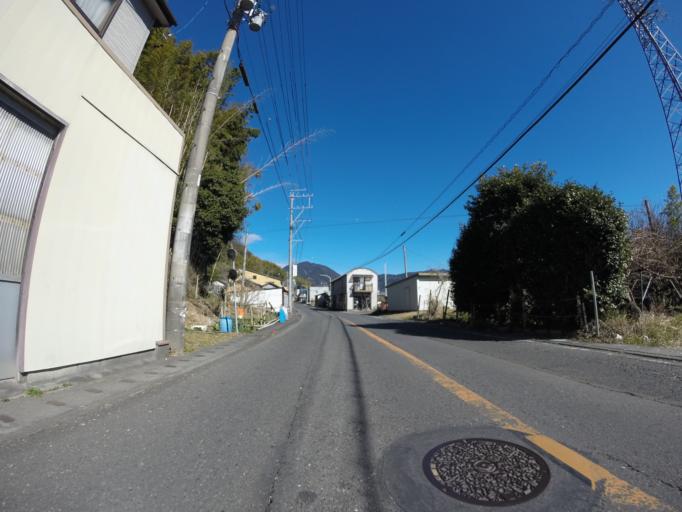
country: JP
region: Shizuoka
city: Shizuoka-shi
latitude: 35.0153
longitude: 138.3849
